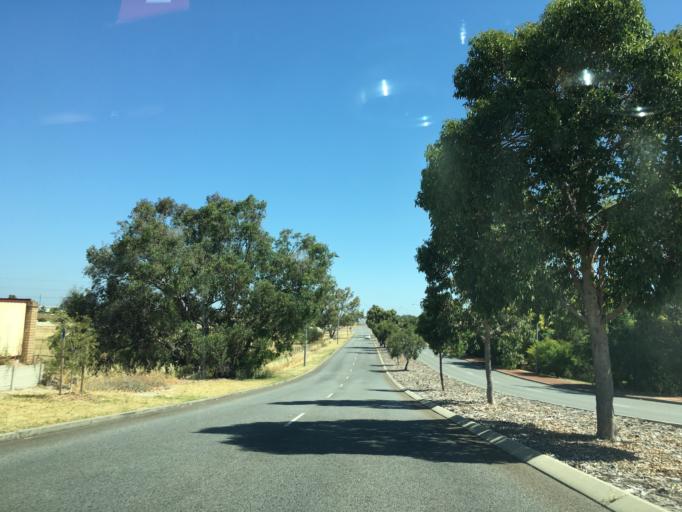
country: AU
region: Western Australia
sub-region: Canning
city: Canning Vale
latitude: -32.0510
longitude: 115.9043
